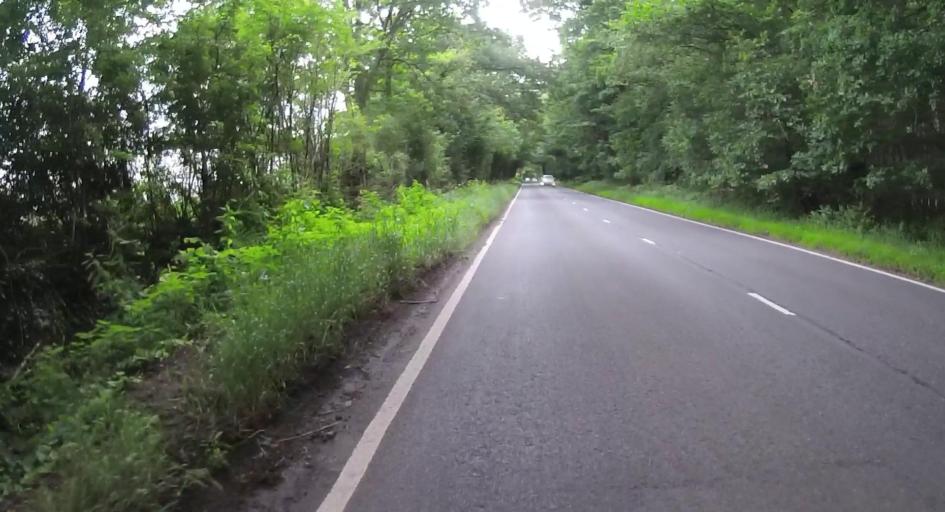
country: GB
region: England
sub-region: Bracknell Forest
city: Crowthorne
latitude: 51.3873
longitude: -0.8159
